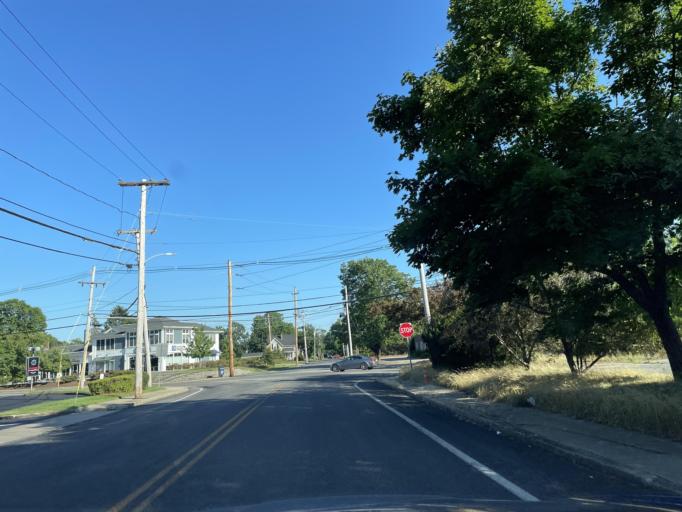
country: US
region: Massachusetts
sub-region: Bristol County
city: Mansfield
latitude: 42.0310
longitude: -71.2281
